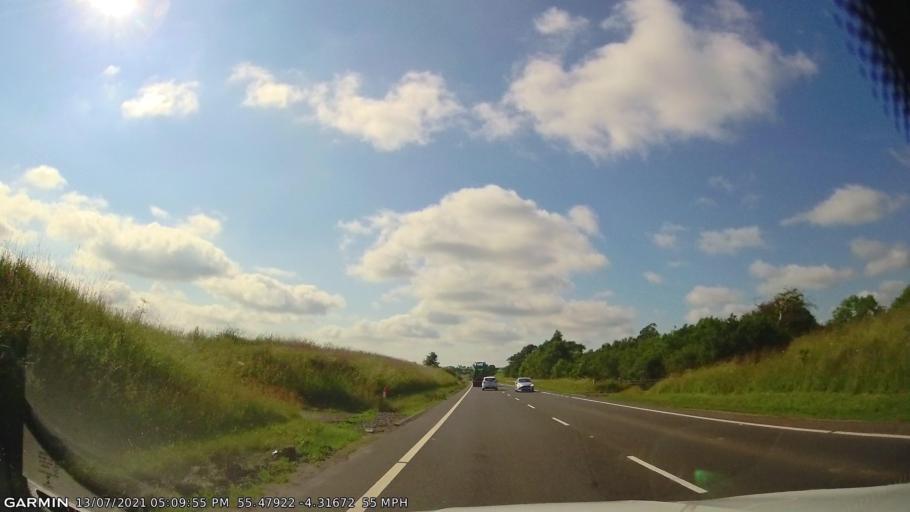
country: GB
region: Scotland
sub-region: East Ayrshire
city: Auchinleck
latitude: 55.4789
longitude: -4.3170
